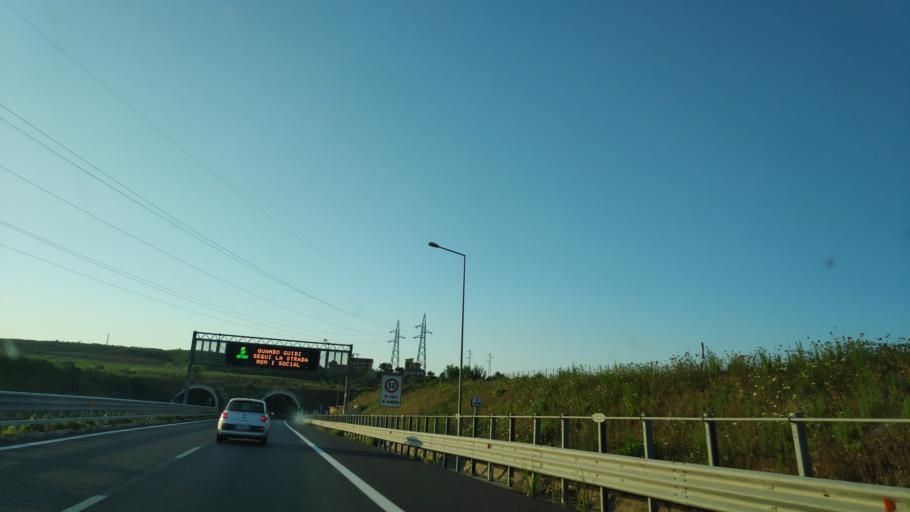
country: IT
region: Calabria
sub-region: Provincia di Reggio Calabria
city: Ceramida-Pellegrina
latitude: 38.3132
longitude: 15.8431
